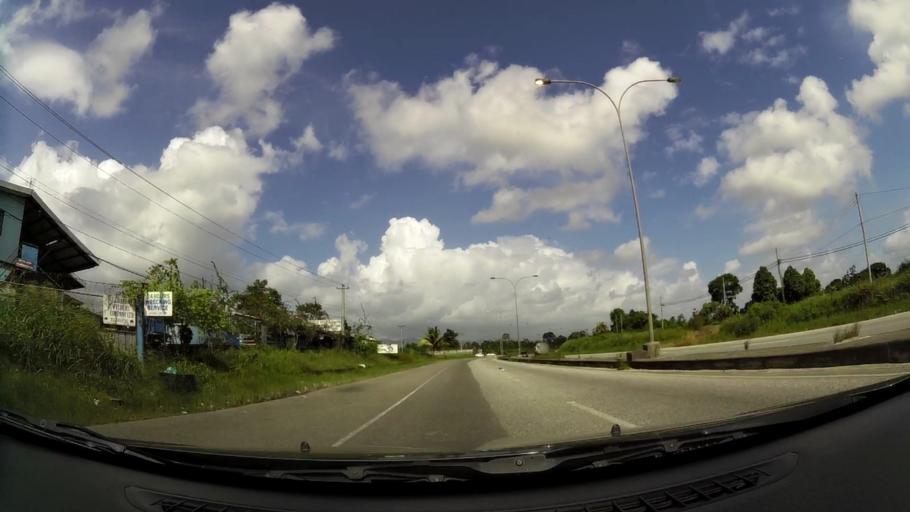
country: TT
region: Borough of Arima
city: Arima
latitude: 10.6192
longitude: -61.2553
